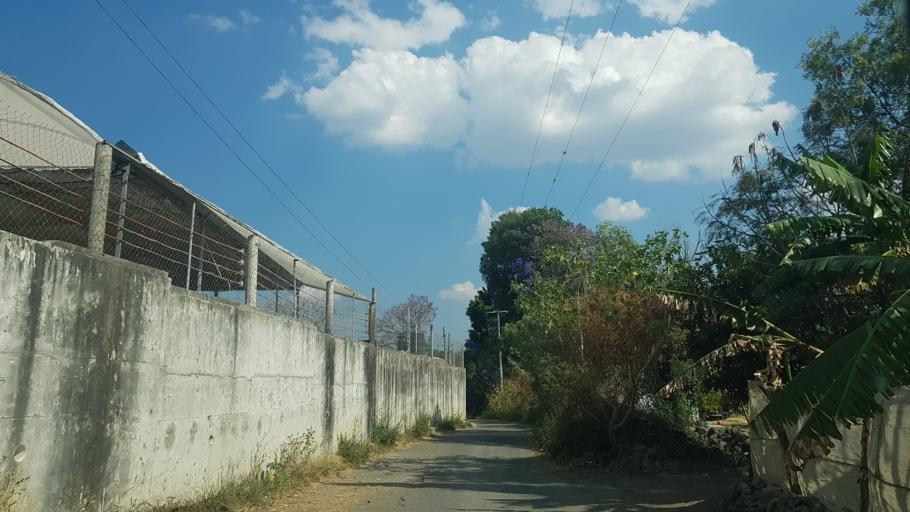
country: MX
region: Puebla
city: Atlixco
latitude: 18.8747
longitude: -98.4868
